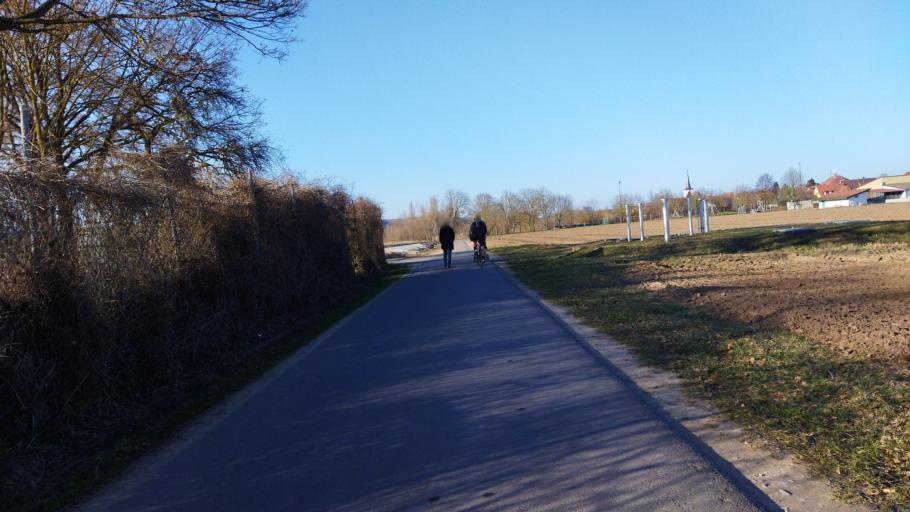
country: DE
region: Bavaria
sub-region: Regierungsbezirk Unterfranken
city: Albertshofen
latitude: 49.7654
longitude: 10.1577
